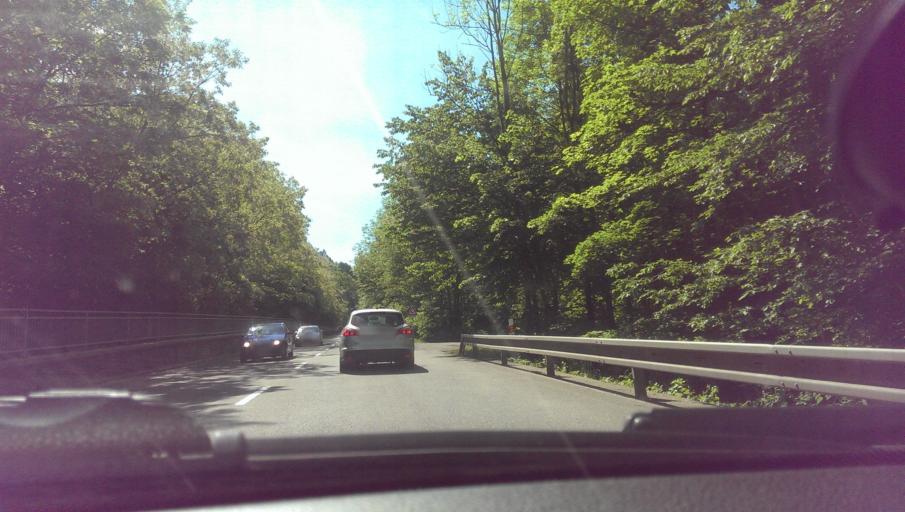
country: CZ
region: Zlin
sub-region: Okres Zlin
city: Zlin
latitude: 49.2164
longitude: 17.6608
